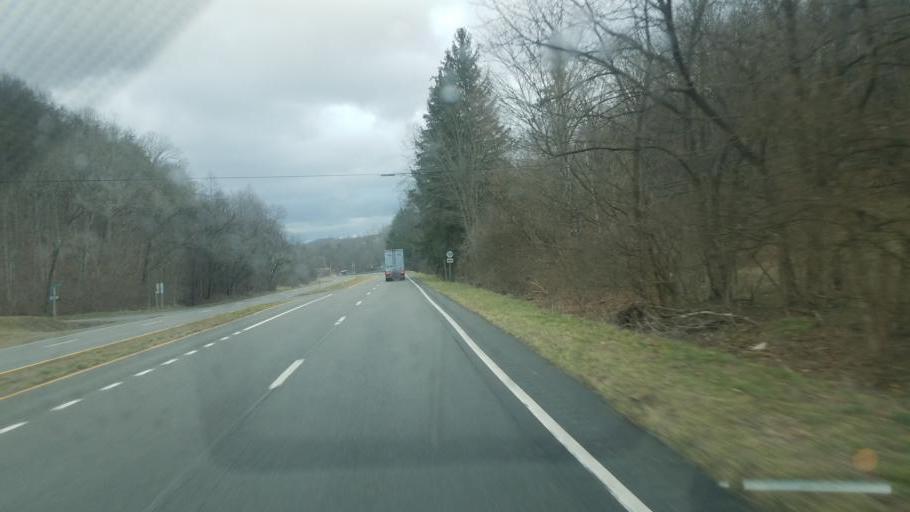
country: US
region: Virginia
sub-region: Giles County
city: Pearisburg
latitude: 37.2732
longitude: -80.7362
